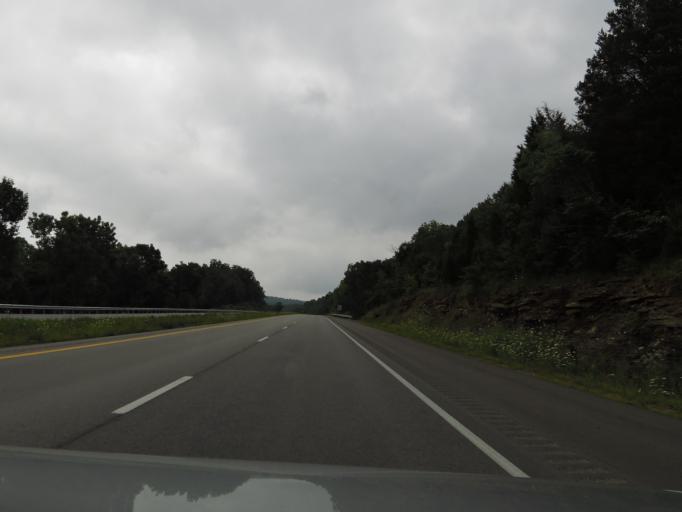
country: US
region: Kentucky
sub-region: Grayson County
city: Leitchfield
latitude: 37.4191
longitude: -86.4001
